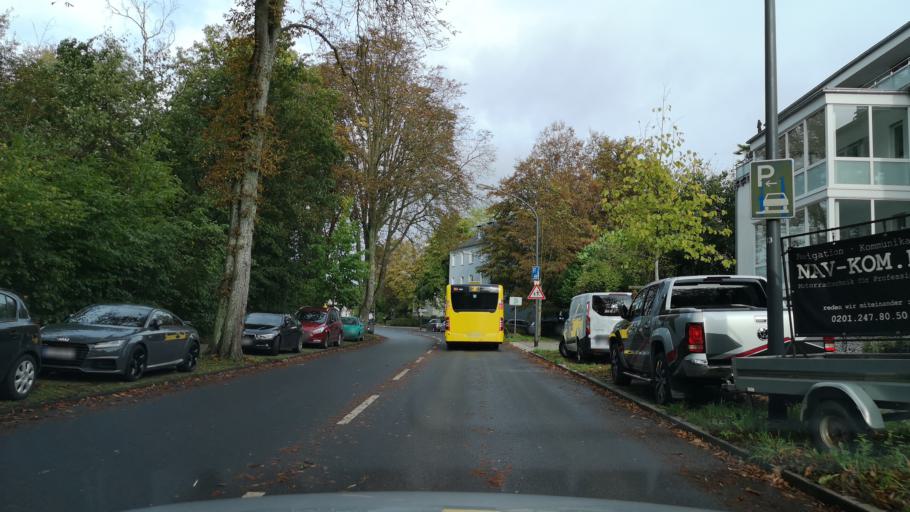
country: DE
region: North Rhine-Westphalia
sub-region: Regierungsbezirk Dusseldorf
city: Velbert
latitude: 51.3847
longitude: 7.0286
